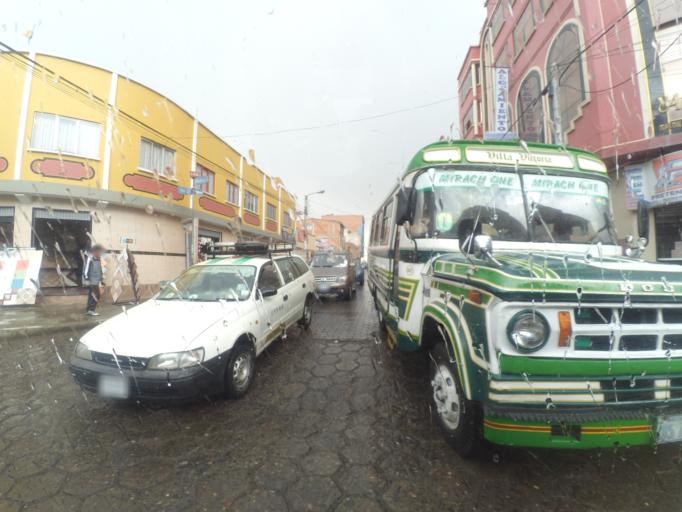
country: BO
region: La Paz
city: La Paz
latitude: -16.5144
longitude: -68.1648
